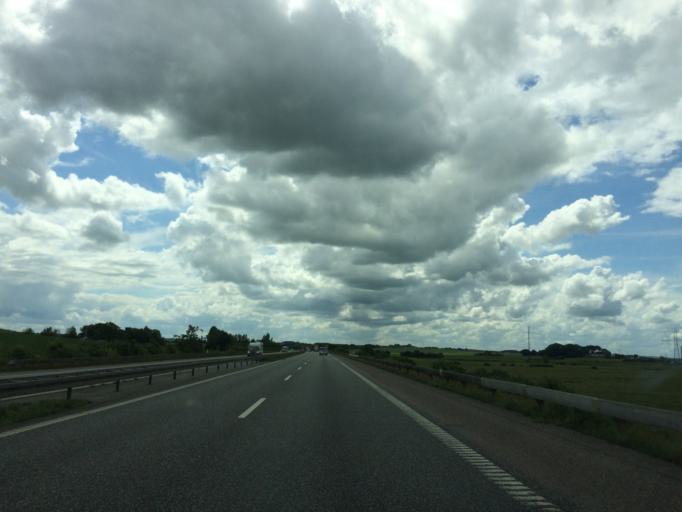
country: DK
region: North Denmark
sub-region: Rebild Kommune
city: Stovring
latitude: 56.8231
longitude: 9.7214
